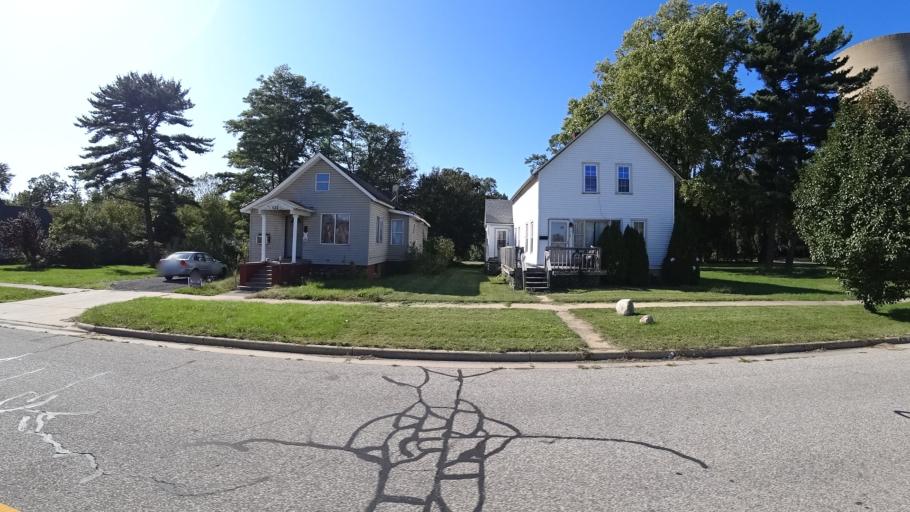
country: US
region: Indiana
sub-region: LaPorte County
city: Michigan City
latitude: 41.7138
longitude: -86.9124
